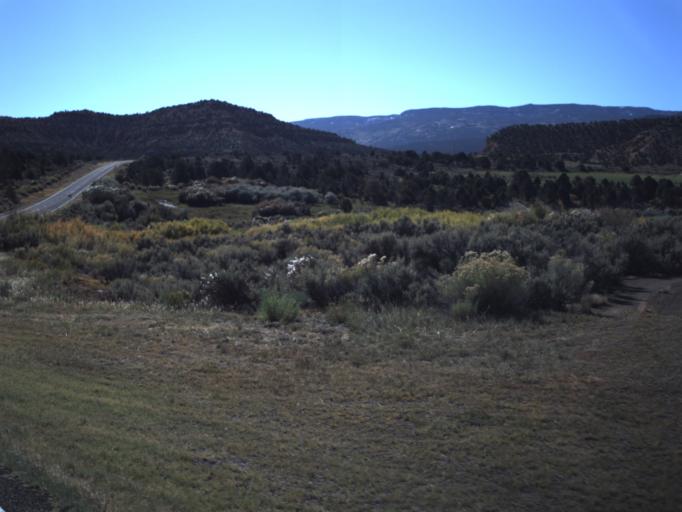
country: US
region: Utah
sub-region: Wayne County
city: Loa
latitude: 38.2712
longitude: -111.3764
